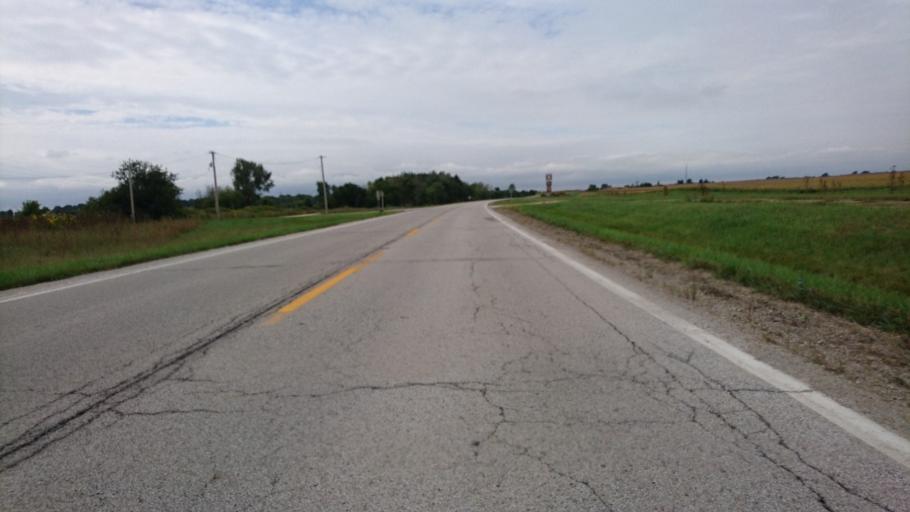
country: US
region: Illinois
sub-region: Livingston County
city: Odell
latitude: 41.0175
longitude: -88.5123
